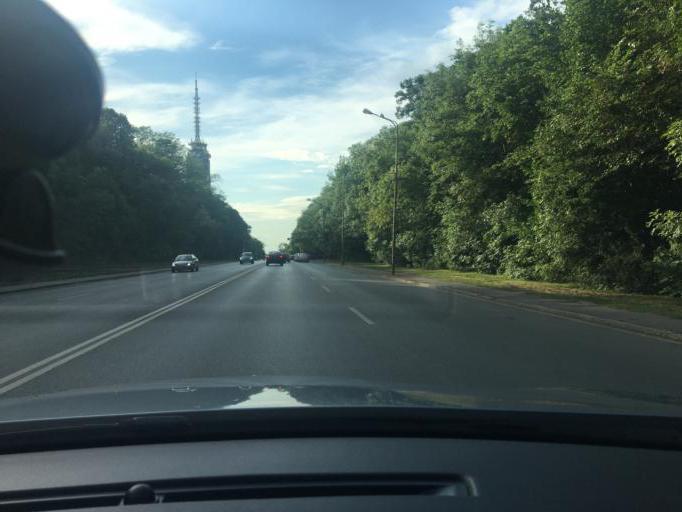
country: BG
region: Sofia-Capital
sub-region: Stolichna Obshtina
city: Sofia
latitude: 42.6746
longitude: 23.3455
